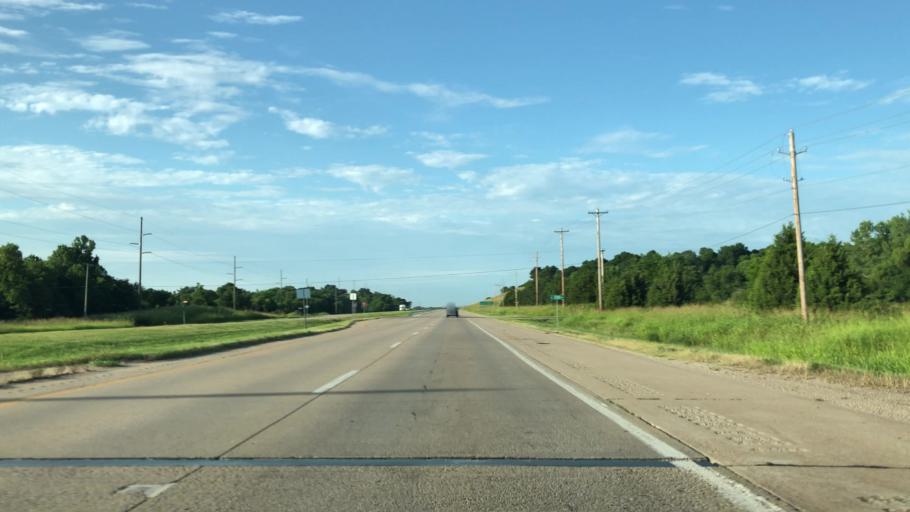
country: US
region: Oklahoma
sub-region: Washington County
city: Bartlesville
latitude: 36.5553
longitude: -95.9295
